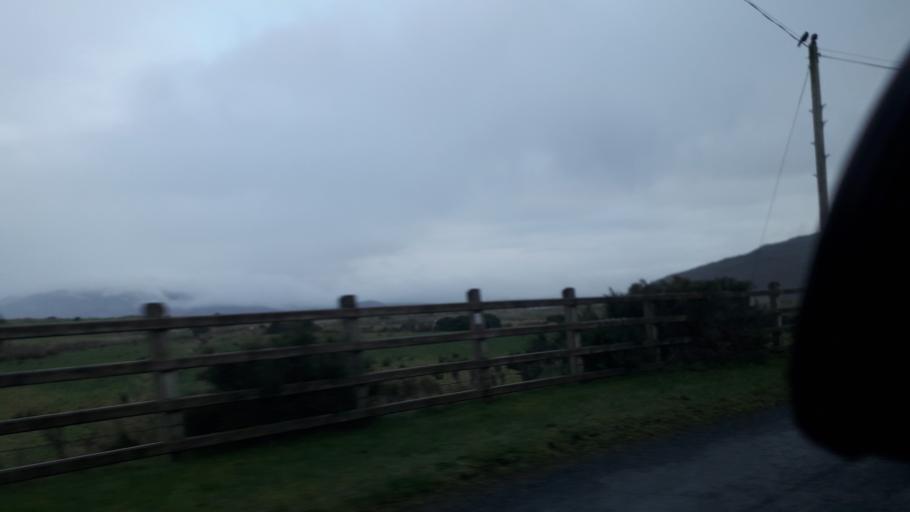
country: IE
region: Ulster
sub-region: County Donegal
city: Ramelton
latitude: 55.1922
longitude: -7.6241
